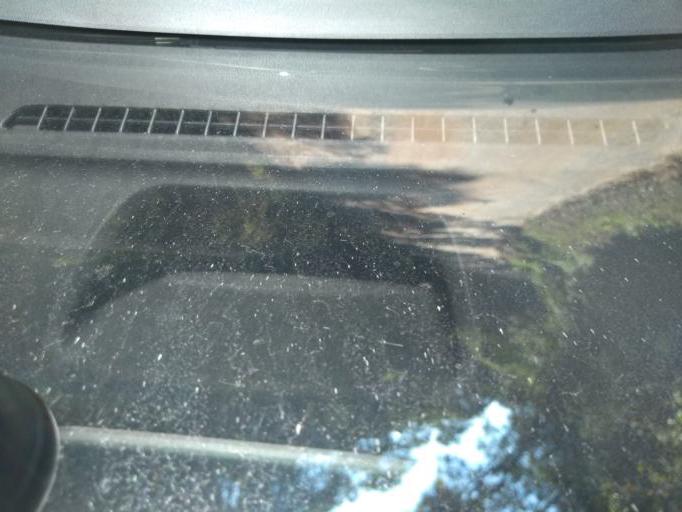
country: BR
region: Sao Paulo
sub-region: Rio Grande Da Serra
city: Rio Grande da Serra
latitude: -23.7626
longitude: -46.4725
